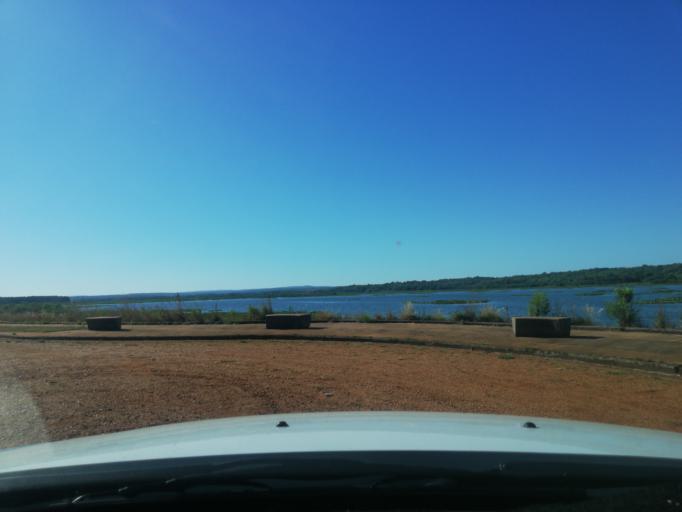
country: AR
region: Misiones
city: Garupa
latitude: -27.4839
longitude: -55.7892
